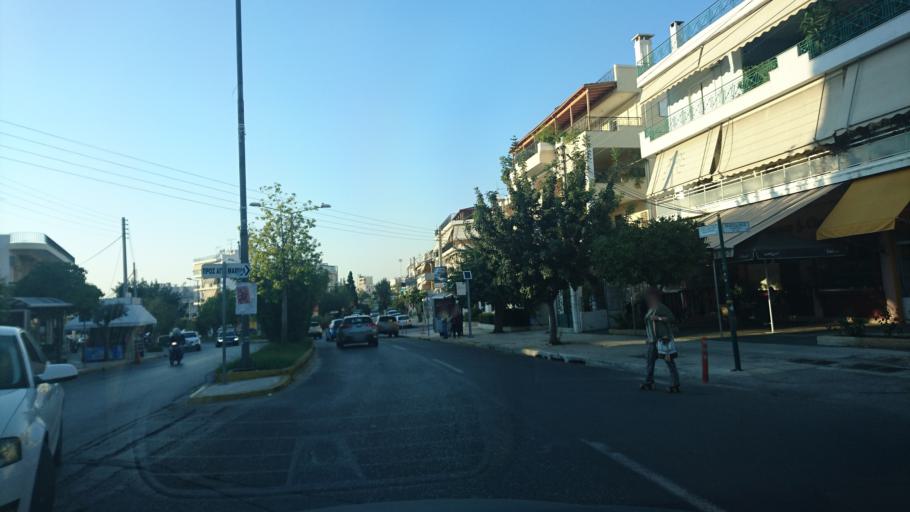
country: GR
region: Attica
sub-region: Nomarchia Athinas
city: Ilioupoli
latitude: 37.9393
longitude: 23.7565
